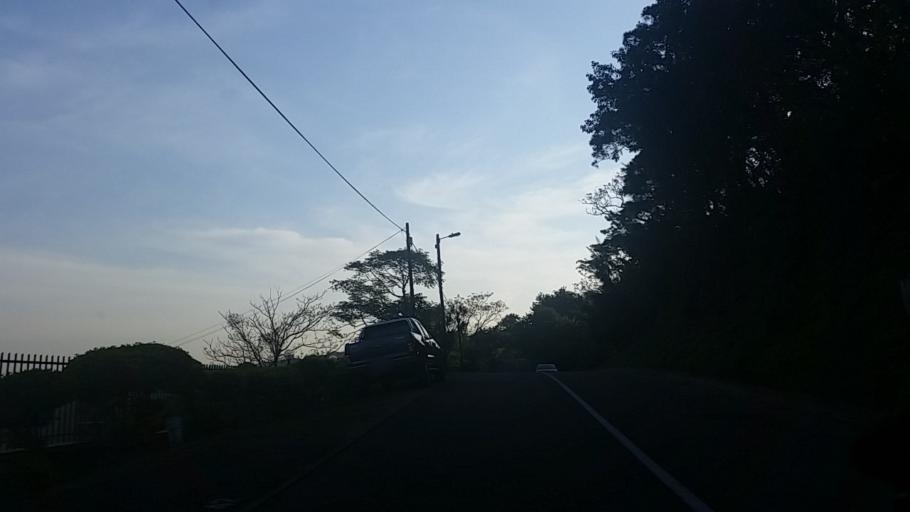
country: ZA
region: KwaZulu-Natal
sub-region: eThekwini Metropolitan Municipality
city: Berea
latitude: -29.8493
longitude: 30.9186
